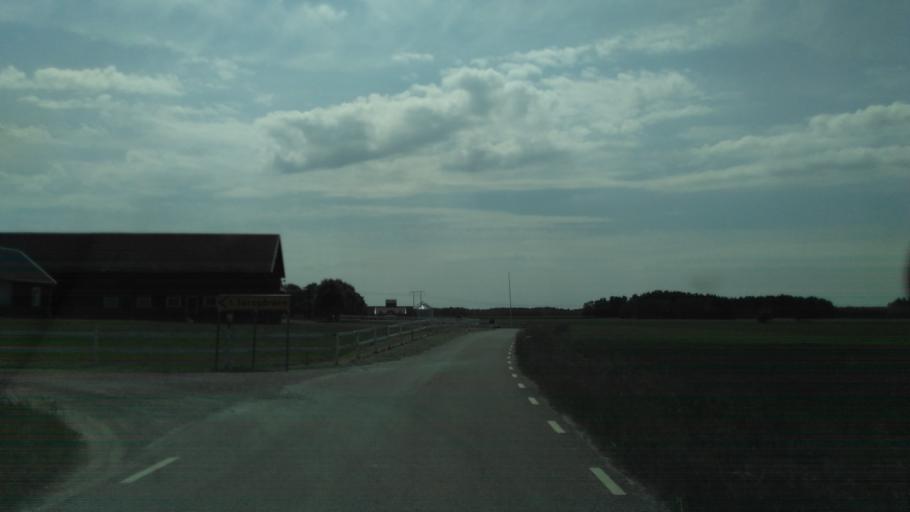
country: SE
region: Vaestra Goetaland
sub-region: Grastorps Kommun
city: Graestorp
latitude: 58.3895
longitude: 12.7911
